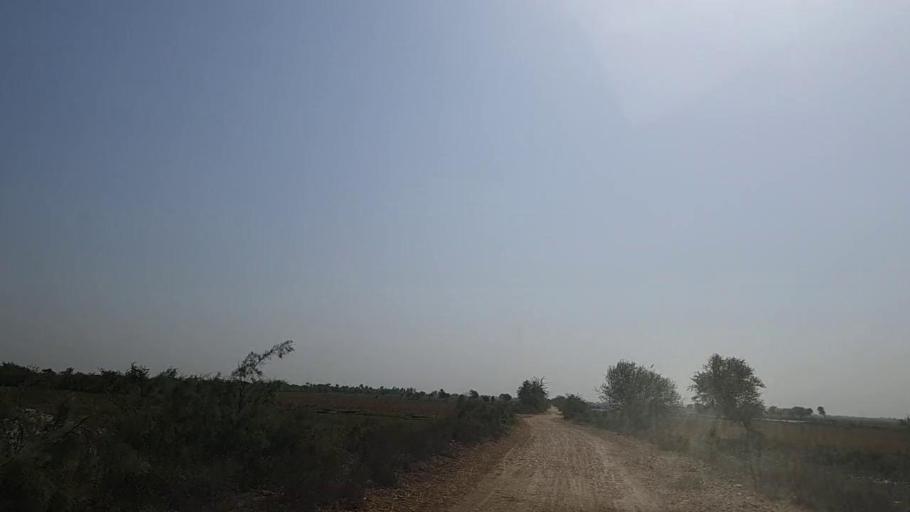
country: PK
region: Sindh
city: Daro Mehar
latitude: 24.7164
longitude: 68.1180
